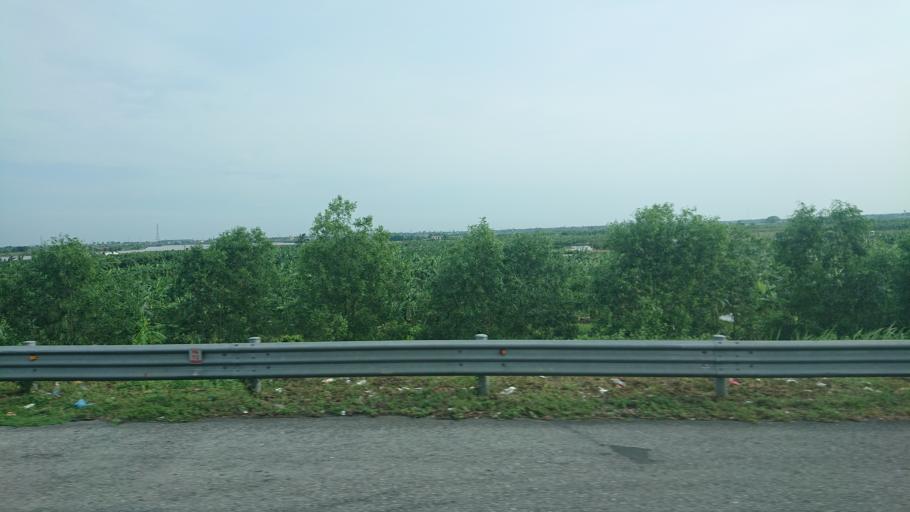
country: VN
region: Hai Phong
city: An Lao
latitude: 20.8094
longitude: 106.5085
